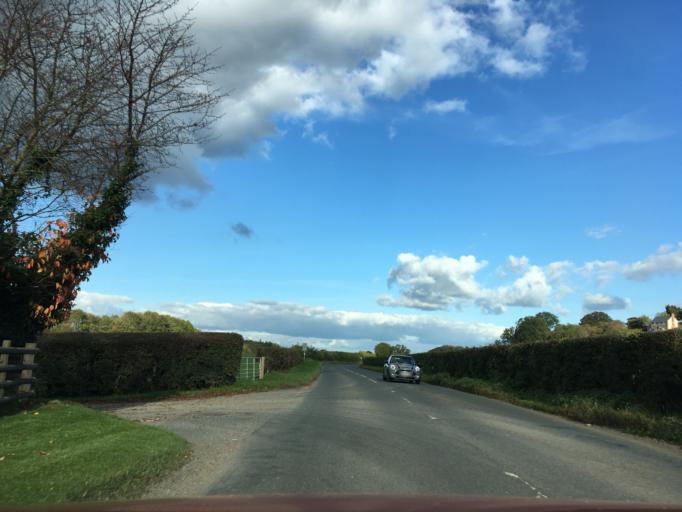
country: GB
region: Wales
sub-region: Sir Powys
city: Hay
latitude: 52.0509
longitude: -3.1788
